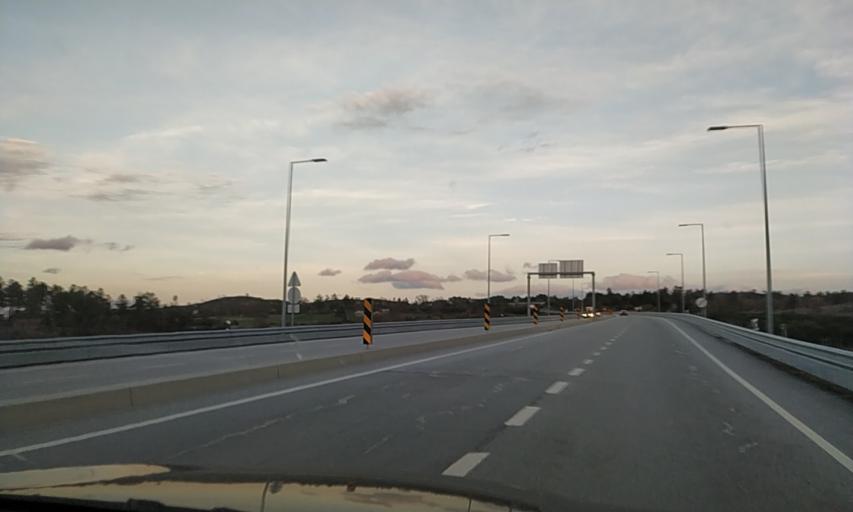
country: PT
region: Braganca
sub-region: Carrazeda de Ansiaes
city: Carrazeda de Anciaes
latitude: 41.2559
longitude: -7.2697
